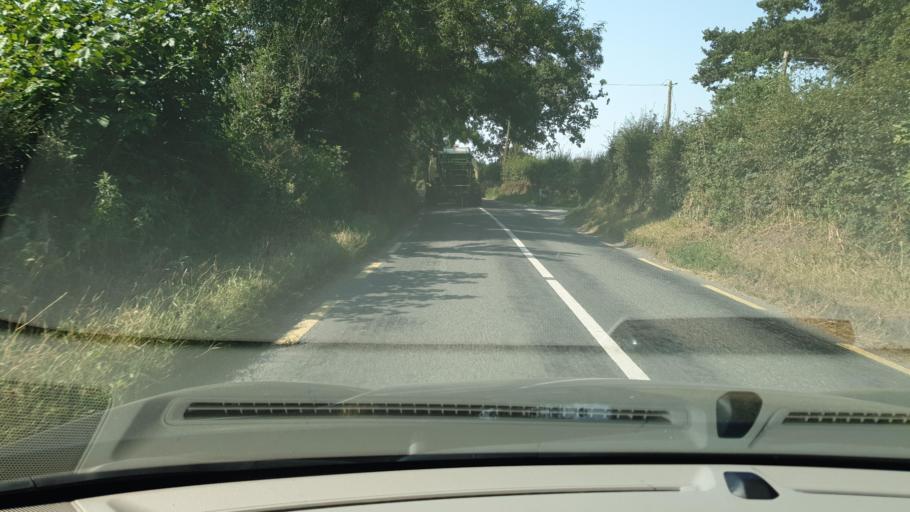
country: IE
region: Leinster
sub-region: An Mhi
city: Athboy
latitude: 53.5871
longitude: -6.8563
